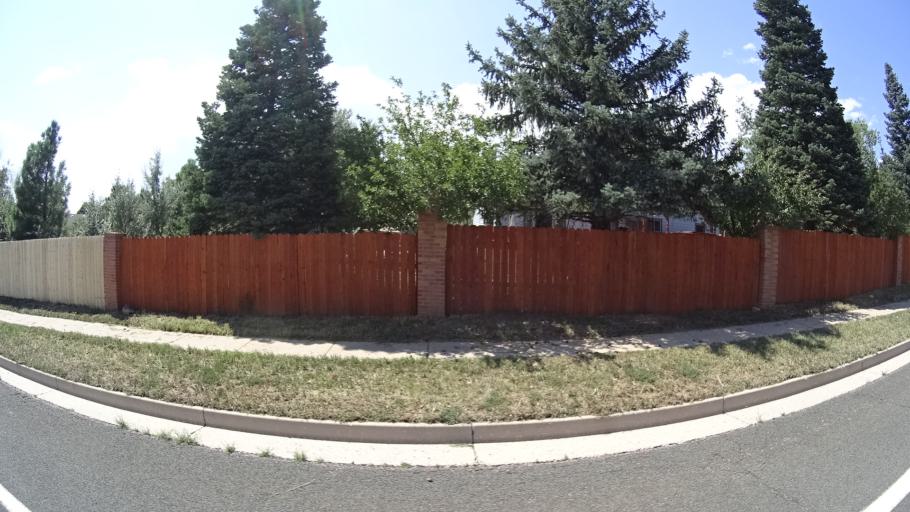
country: US
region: Colorado
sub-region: El Paso County
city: Manitou Springs
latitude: 38.9078
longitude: -104.8731
